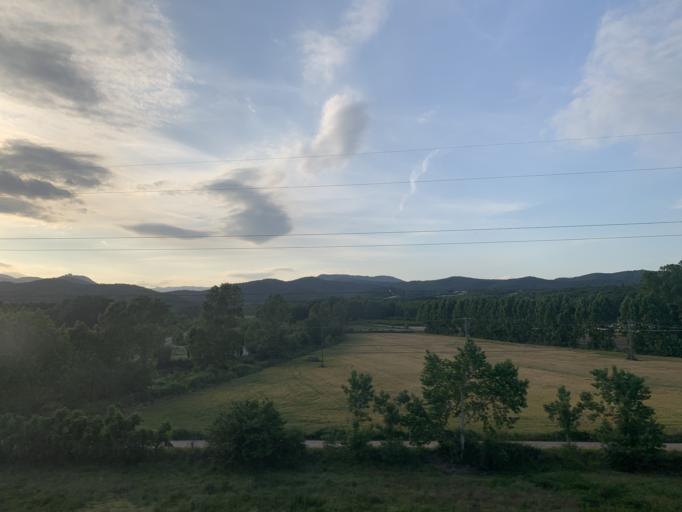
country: ES
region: Catalonia
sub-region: Provincia de Girona
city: Hostalric
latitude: 41.7444
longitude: 2.6182
